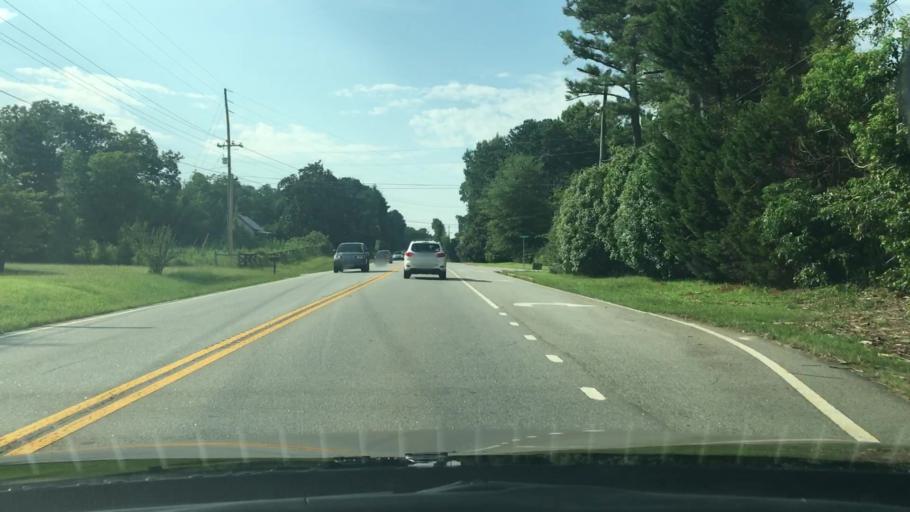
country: US
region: Georgia
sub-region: Fayette County
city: Peachtree City
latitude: 33.3972
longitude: -84.6795
